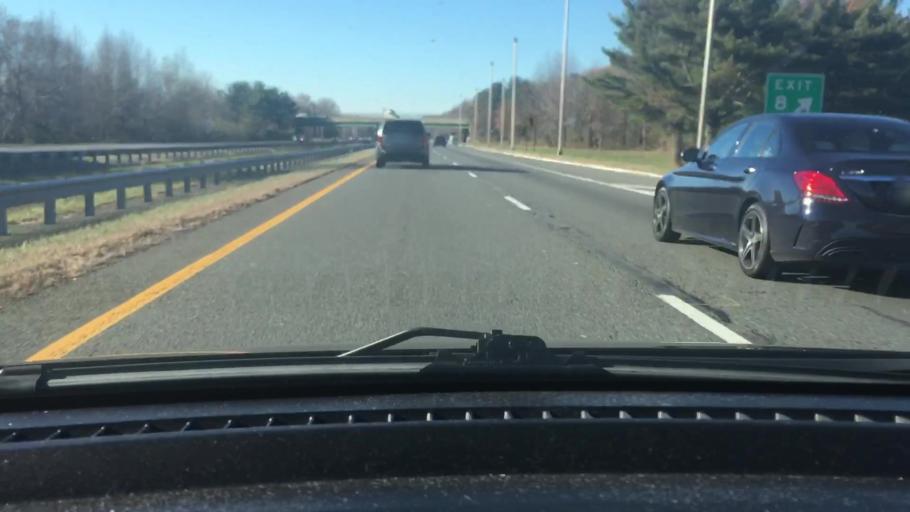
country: US
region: New Jersey
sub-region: Monmouth County
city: Allentown
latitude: 40.1850
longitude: -74.5674
